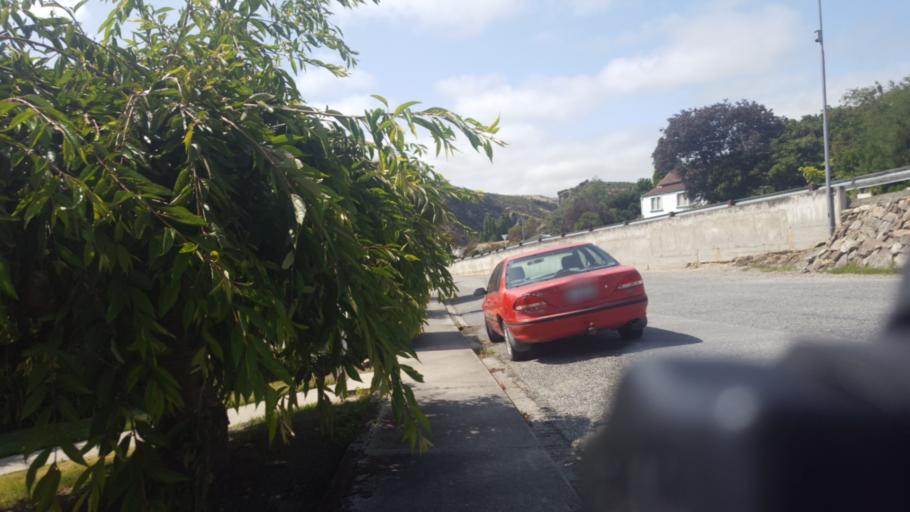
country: NZ
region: Otago
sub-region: Queenstown-Lakes District
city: Kingston
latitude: -45.5425
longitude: 169.3187
